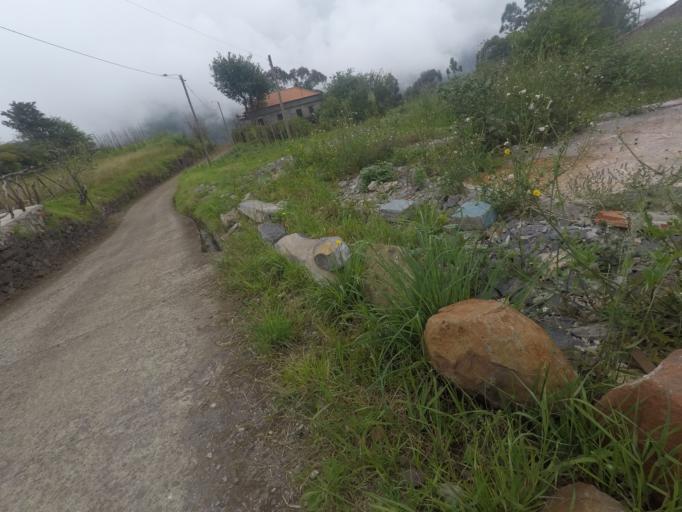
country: PT
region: Madeira
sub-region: Santana
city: Santana
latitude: 32.7536
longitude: -16.8723
